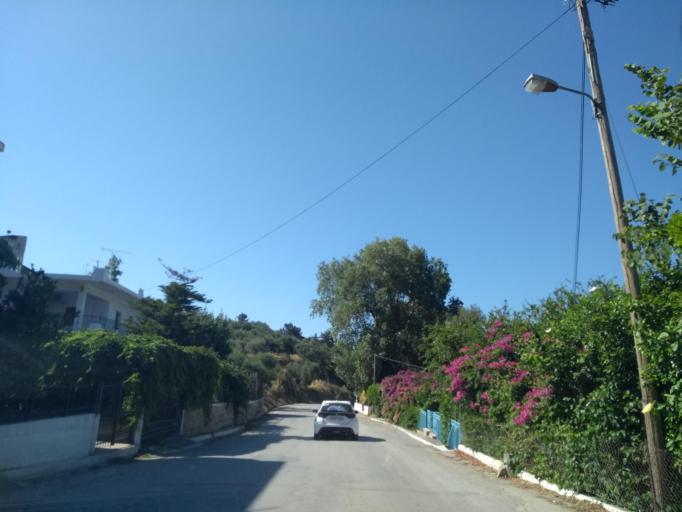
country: GR
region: Crete
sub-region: Nomos Chanias
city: Kissamos
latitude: 35.4286
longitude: 23.6875
